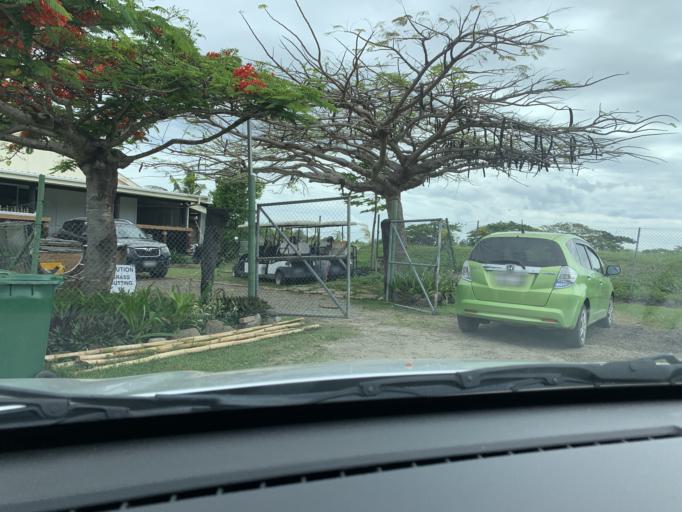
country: FJ
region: Western
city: Nadi
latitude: -17.7819
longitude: 177.3798
